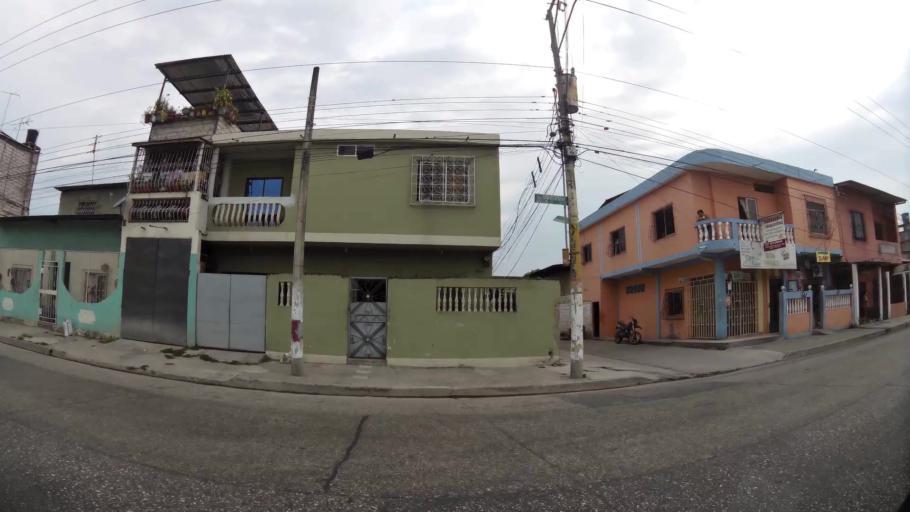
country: EC
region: Guayas
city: Guayaquil
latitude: -2.2487
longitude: -79.8800
